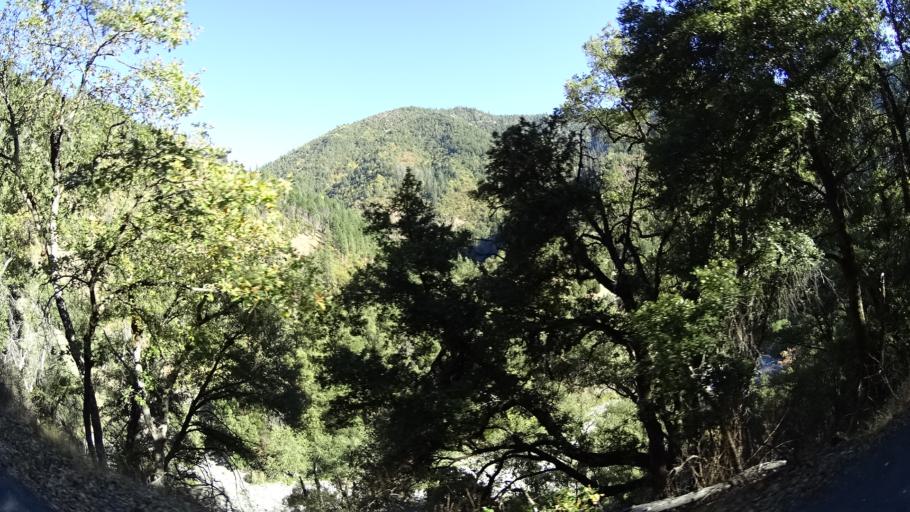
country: US
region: California
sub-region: Humboldt County
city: Willow Creek
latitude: 41.2834
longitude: -123.2649
